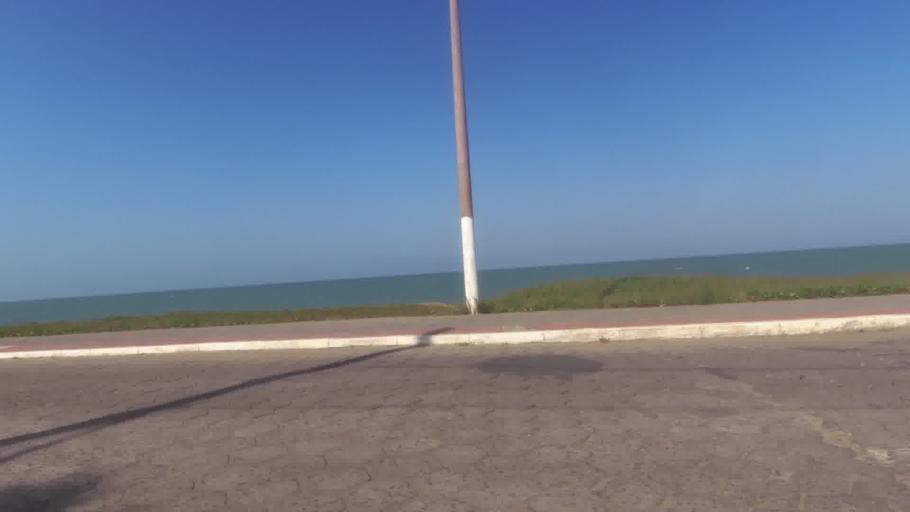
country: BR
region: Espirito Santo
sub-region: Itapemirim
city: Itapemirim
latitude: -21.0181
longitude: -40.8102
